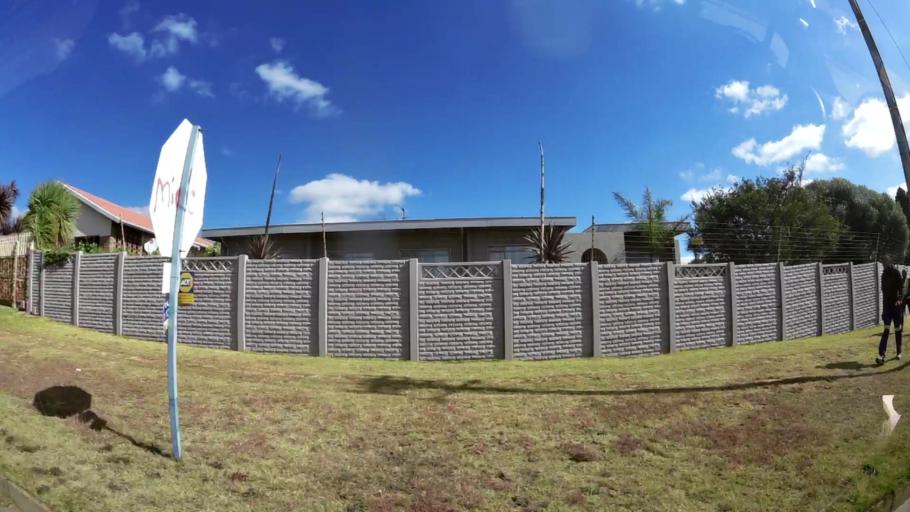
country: ZA
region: Gauteng
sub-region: West Rand District Municipality
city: Krugersdorp
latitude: -26.1209
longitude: 27.8232
